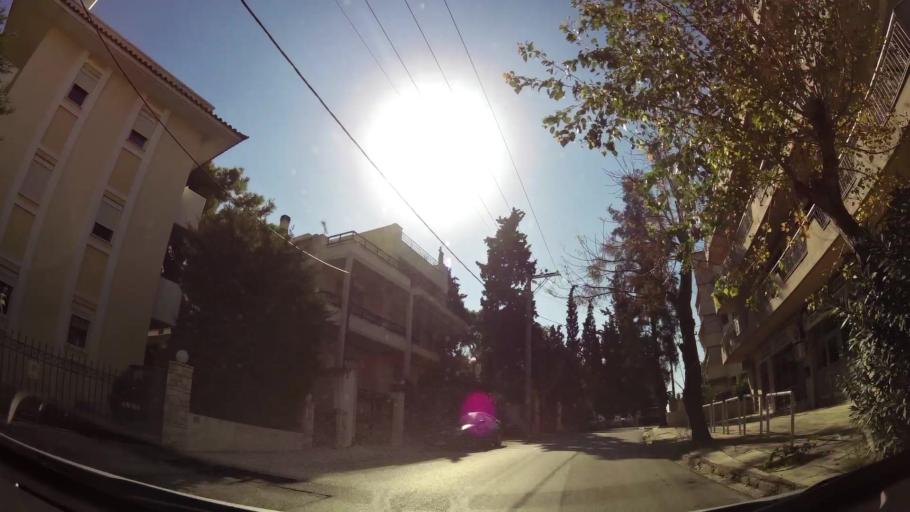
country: GR
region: Attica
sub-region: Nomarchia Athinas
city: Lykovrysi
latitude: 38.0667
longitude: 23.7746
